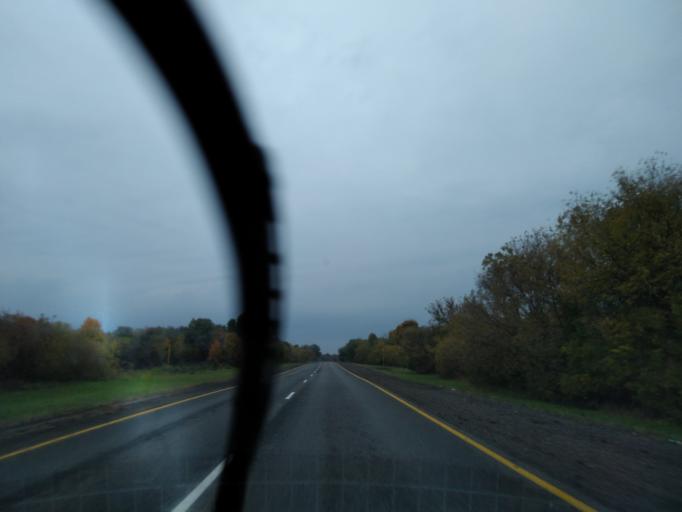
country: RU
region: Lipetsk
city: Zadonsk
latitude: 52.4840
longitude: 38.7614
